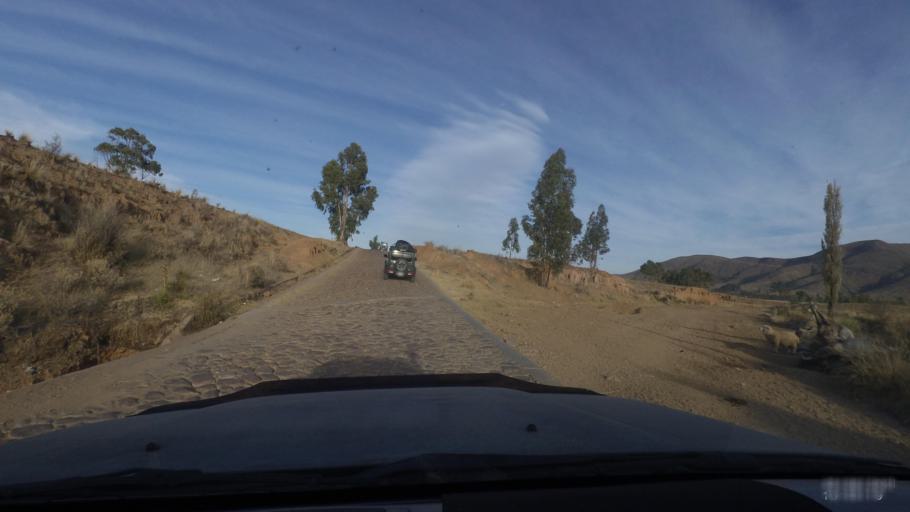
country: BO
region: Cochabamba
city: Arani
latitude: -17.8208
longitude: -65.7744
